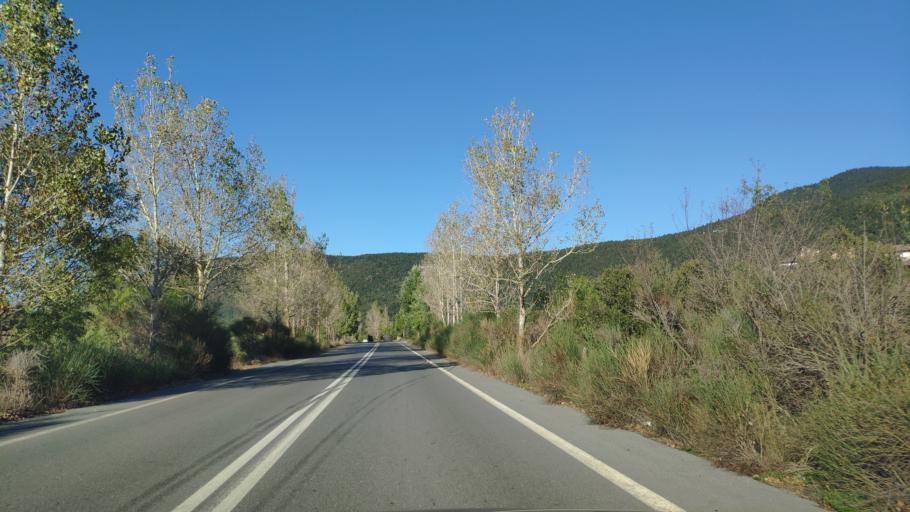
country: GR
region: Peloponnese
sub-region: Nomos Arkadias
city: Langadhia
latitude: 37.6868
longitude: 22.1929
